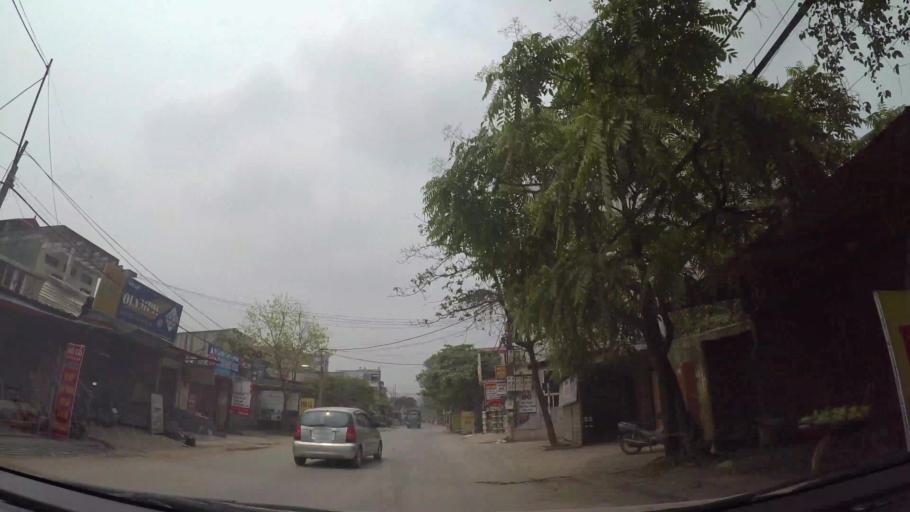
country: VN
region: Ha Noi
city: Cau Dien
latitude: 21.0329
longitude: 105.7390
